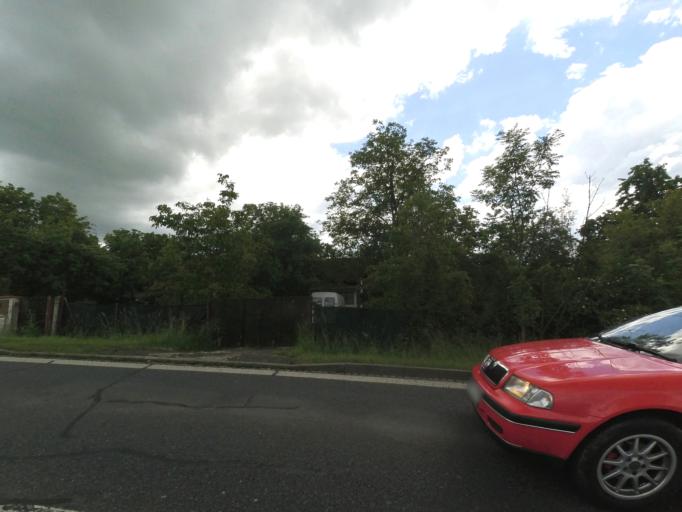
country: CZ
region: Plzensky
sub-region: Okres Domazlice
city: Kdyne
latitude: 49.3917
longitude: 13.0306
